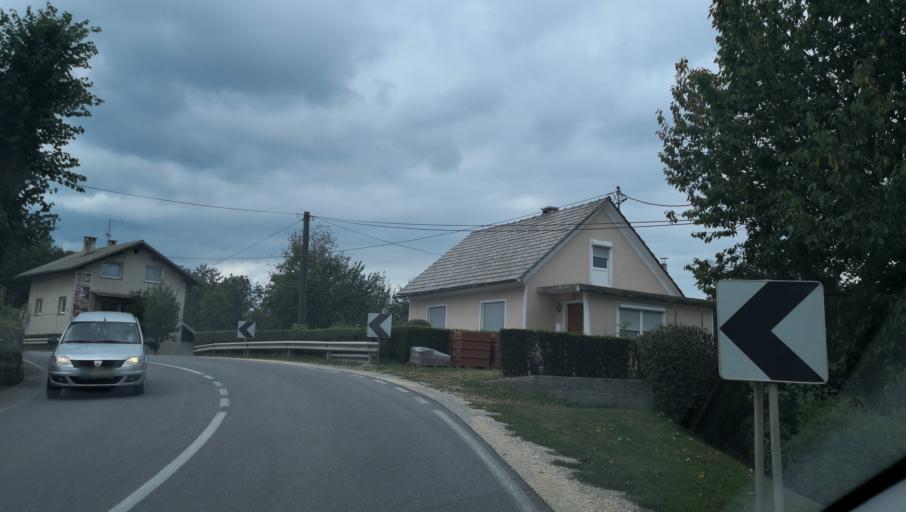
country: SI
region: Novo Mesto
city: Novo Mesto
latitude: 45.7703
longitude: 15.1929
